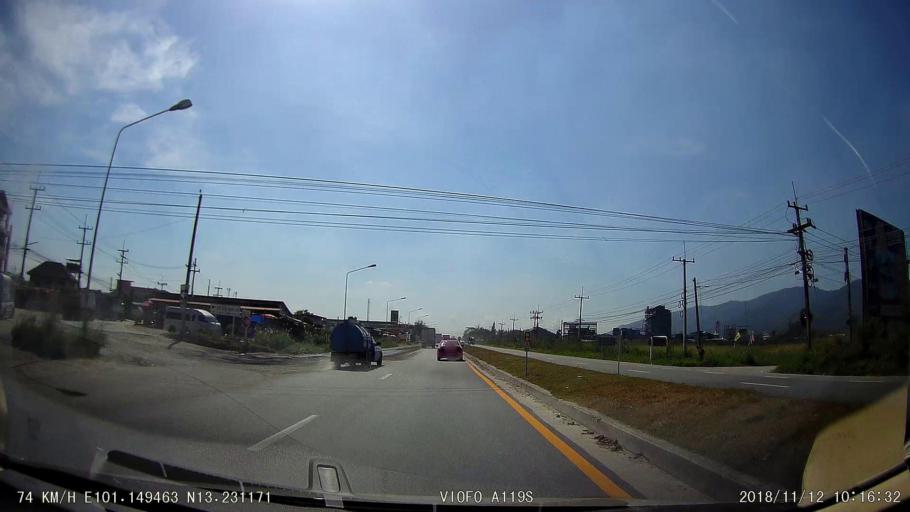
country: TH
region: Chon Buri
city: Ban Bueng
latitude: 13.2309
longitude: 101.1495
